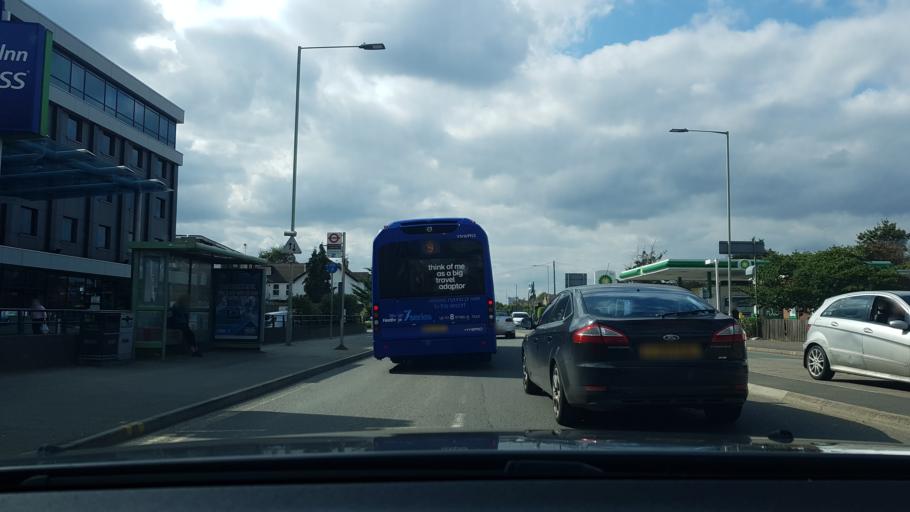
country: GB
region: England
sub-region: Surrey
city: Colnbrook
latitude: 51.4890
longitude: -0.5357
